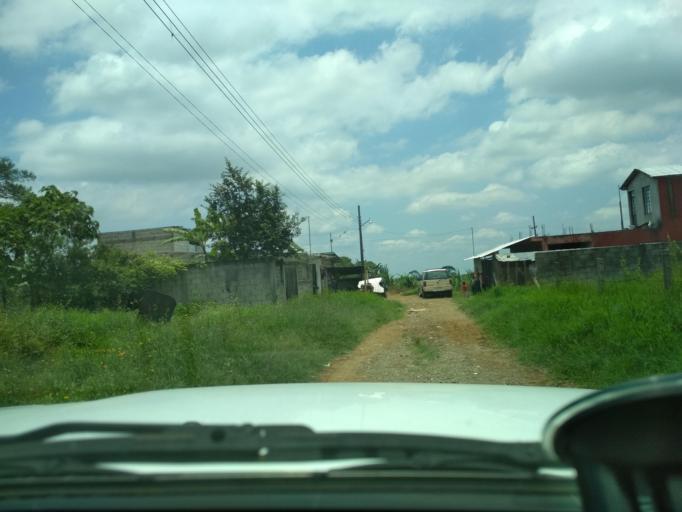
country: MX
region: Veracruz
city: Tocuila
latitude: 18.9502
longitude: -97.0161
